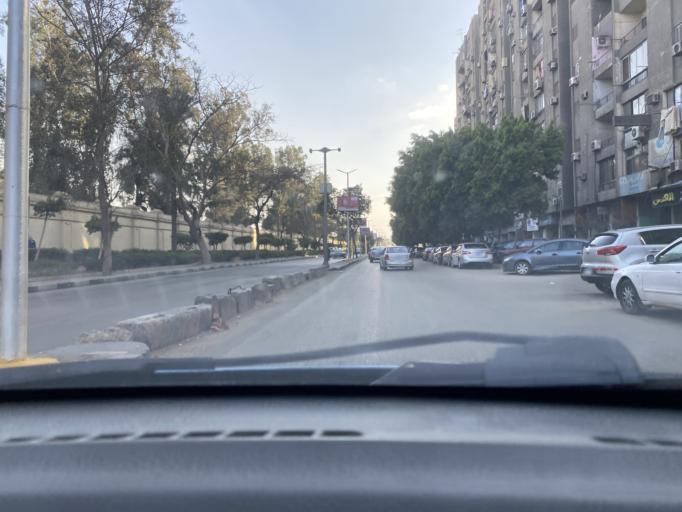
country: EG
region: Muhafazat al Qahirah
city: Cairo
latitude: 30.1007
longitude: 31.3003
